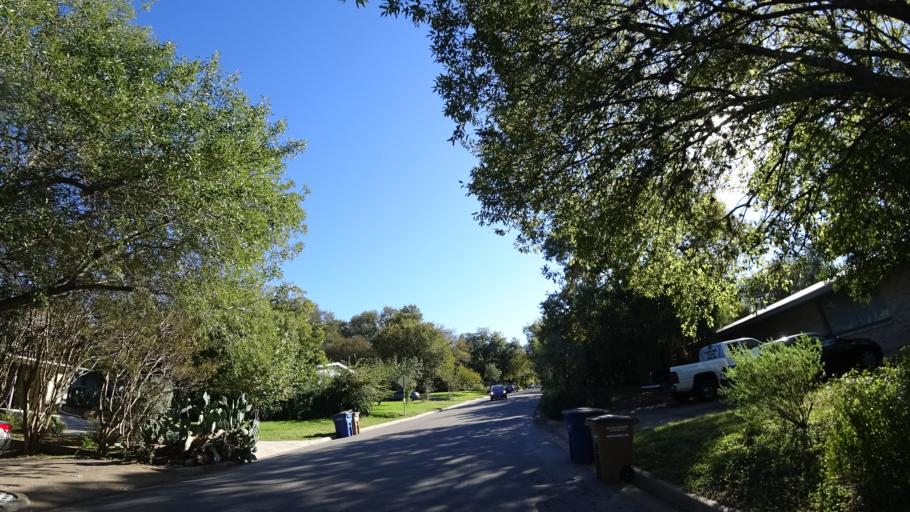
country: US
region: Texas
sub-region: Travis County
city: Rollingwood
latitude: 30.2446
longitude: -97.7858
